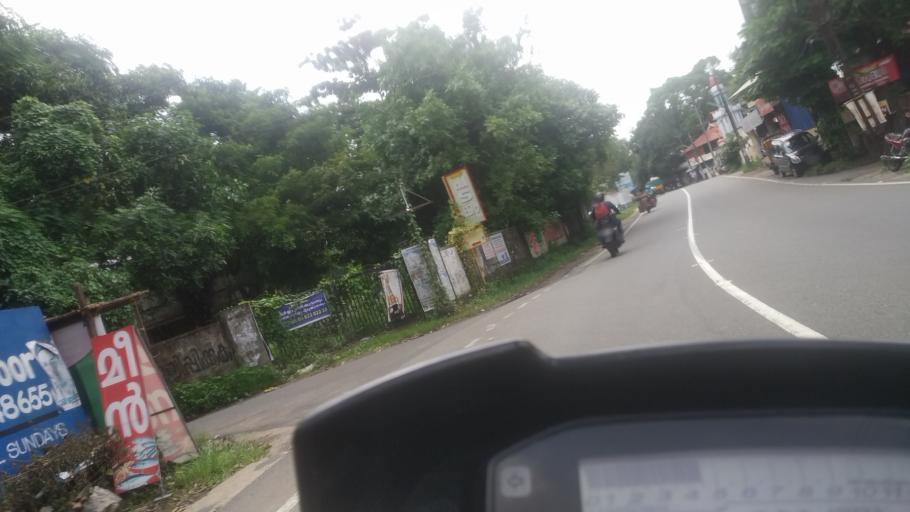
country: IN
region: Kerala
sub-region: Ernakulam
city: Elur
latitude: 10.1315
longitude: 76.2800
